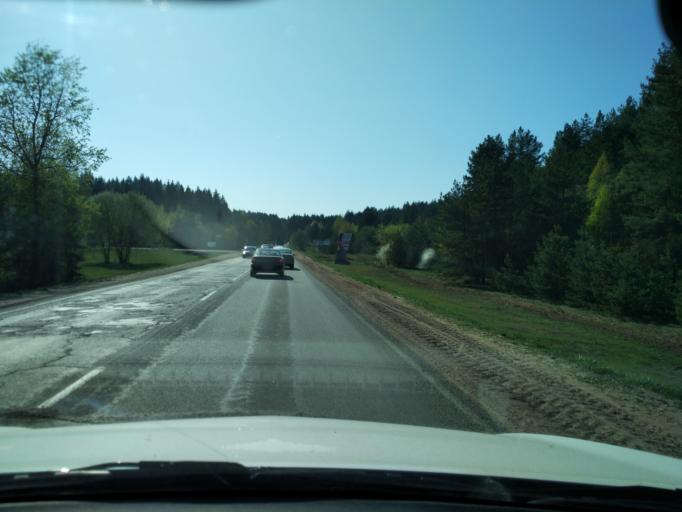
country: BY
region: Minsk
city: Lyeskawka
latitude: 53.9611
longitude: 27.7038
